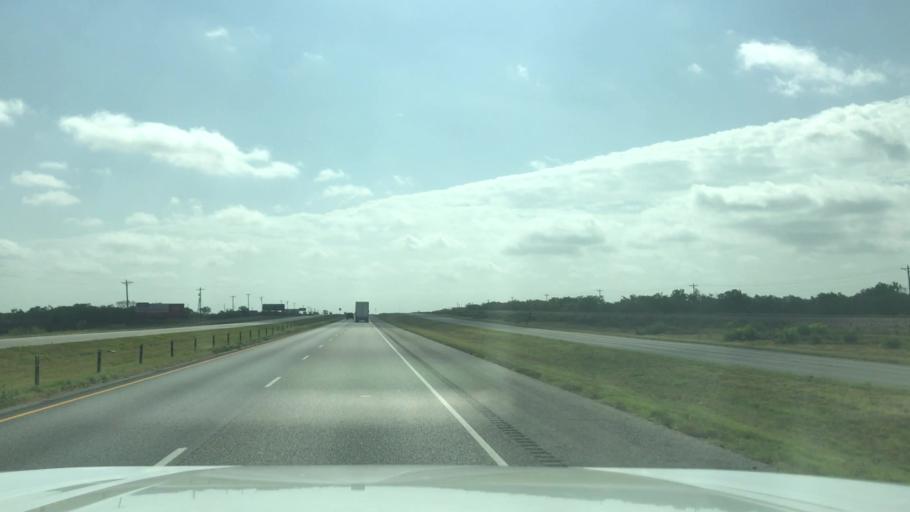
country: US
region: Texas
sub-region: Taylor County
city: Merkel
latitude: 32.4653
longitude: -99.9724
